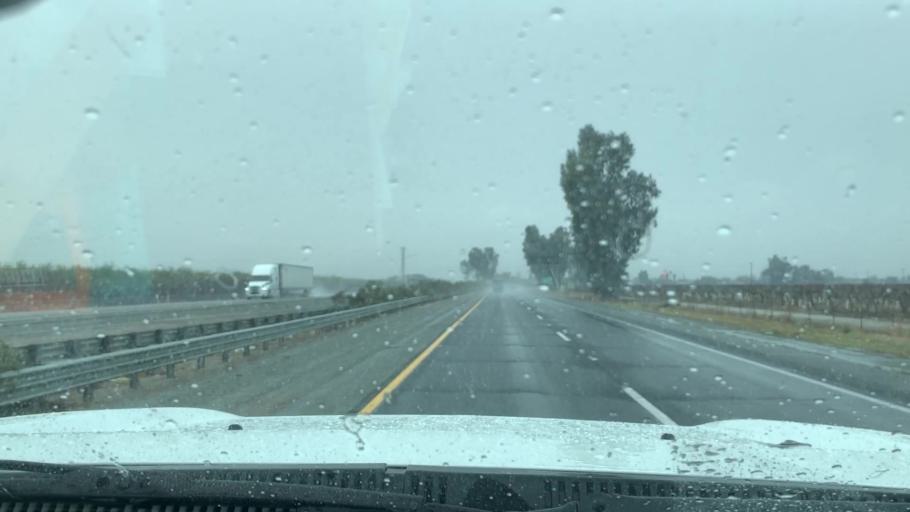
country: US
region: California
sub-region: Tulare County
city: Earlimart
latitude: 35.8667
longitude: -119.2700
